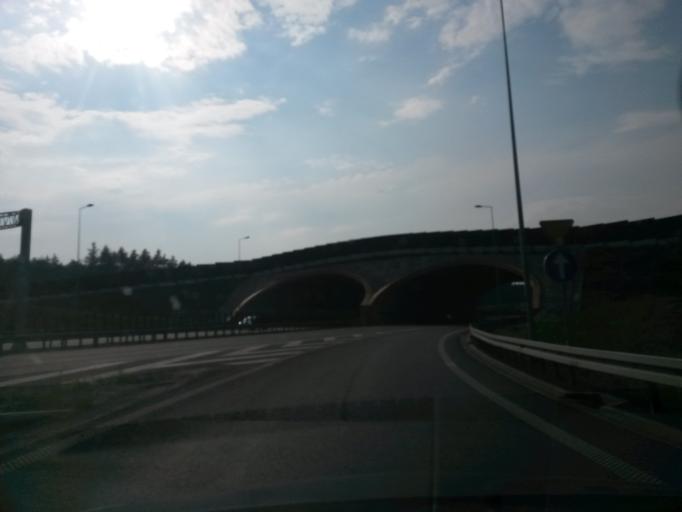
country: PL
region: Lesser Poland Voivodeship
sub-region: Powiat brzeski
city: Jasien
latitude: 49.9921
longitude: 20.5826
